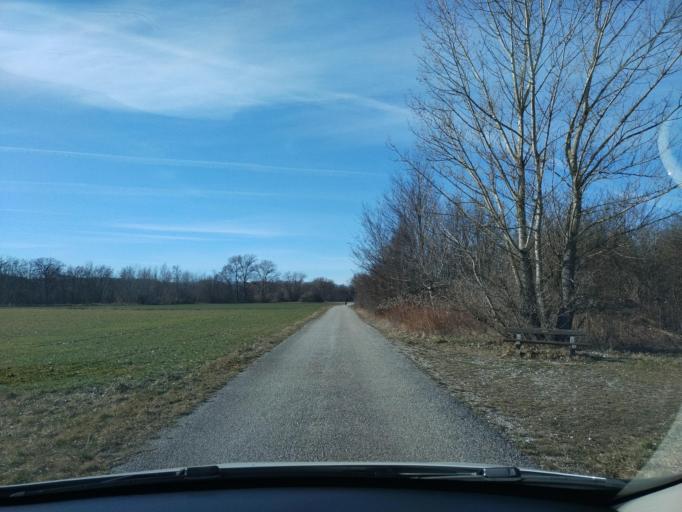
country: AT
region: Lower Austria
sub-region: Politischer Bezirk Neunkirchen
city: Pitten
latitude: 47.7380
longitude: 16.1926
